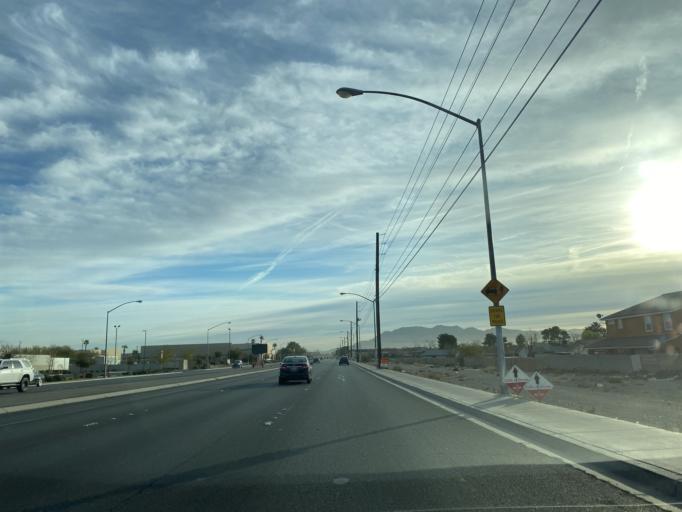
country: US
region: Nevada
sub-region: Clark County
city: Nellis Air Force Base
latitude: 36.2403
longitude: -115.0749
